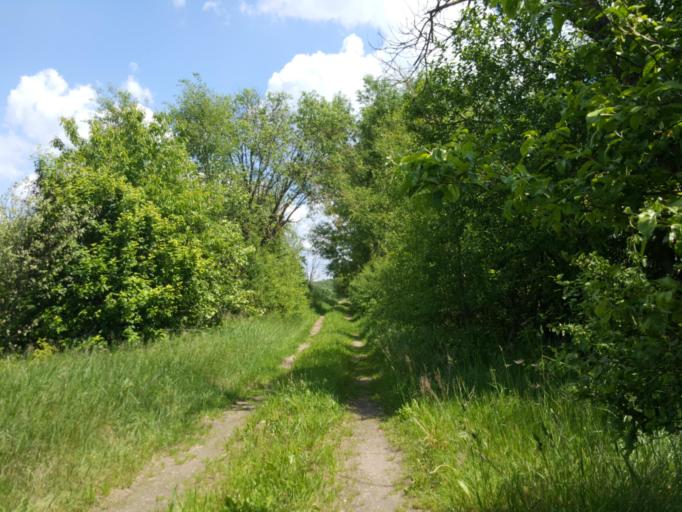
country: BY
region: Brest
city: Kamyanyets
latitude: 52.4390
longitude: 23.7213
